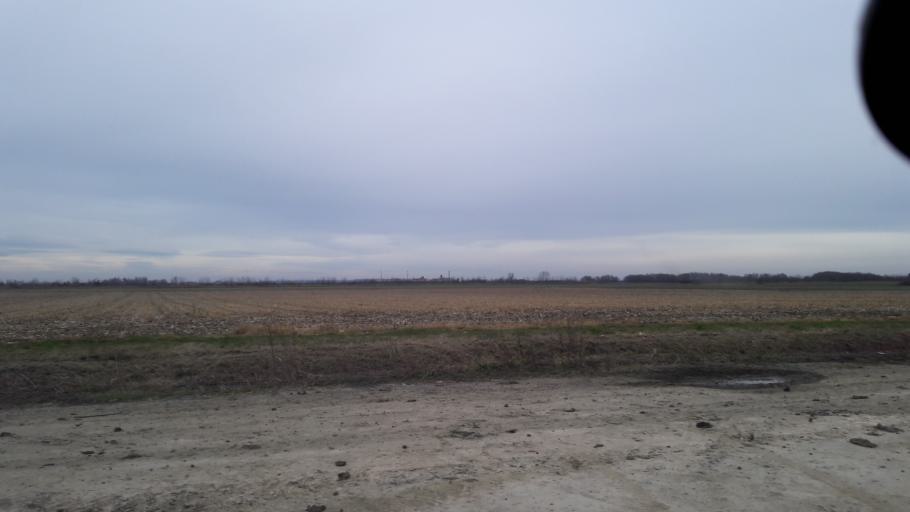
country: HR
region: Osjecko-Baranjska
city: Vladislavci
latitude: 45.4261
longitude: 18.5795
